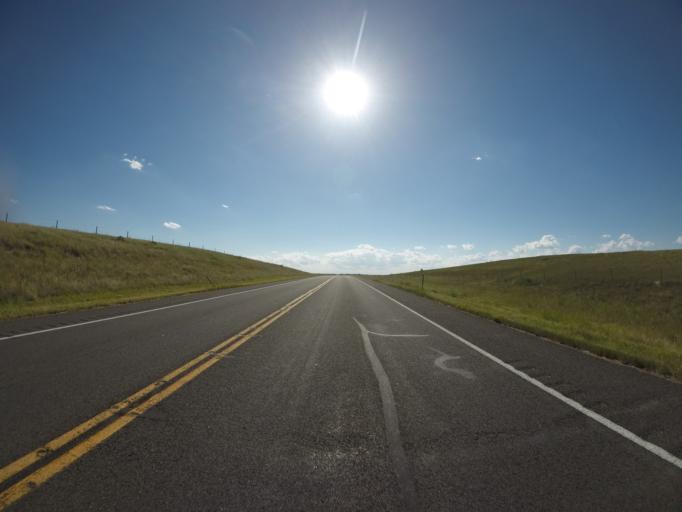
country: US
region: Colorado
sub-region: Morgan County
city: Brush
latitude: 40.6110
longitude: -103.5680
